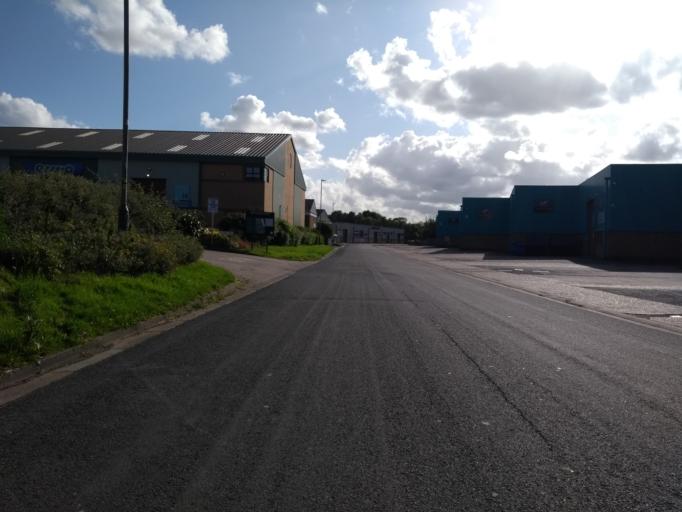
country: GB
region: England
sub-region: Warwickshire
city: Warwick
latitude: 52.2869
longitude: -1.6059
